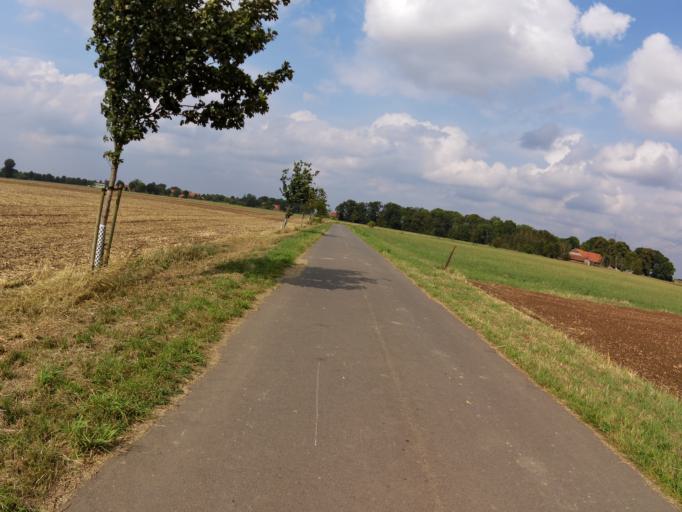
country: DE
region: Lower Saxony
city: Hilgermissen
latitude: 52.8803
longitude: 9.1763
